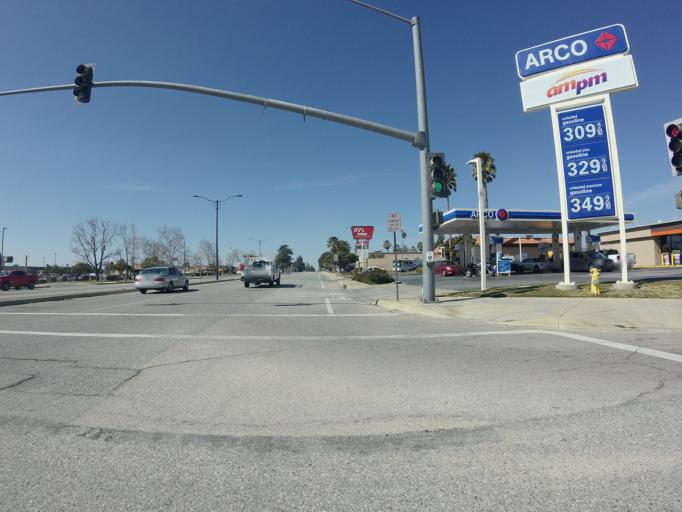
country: US
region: California
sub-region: Riverside County
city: Beaumont
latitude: 33.9295
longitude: -116.9470
